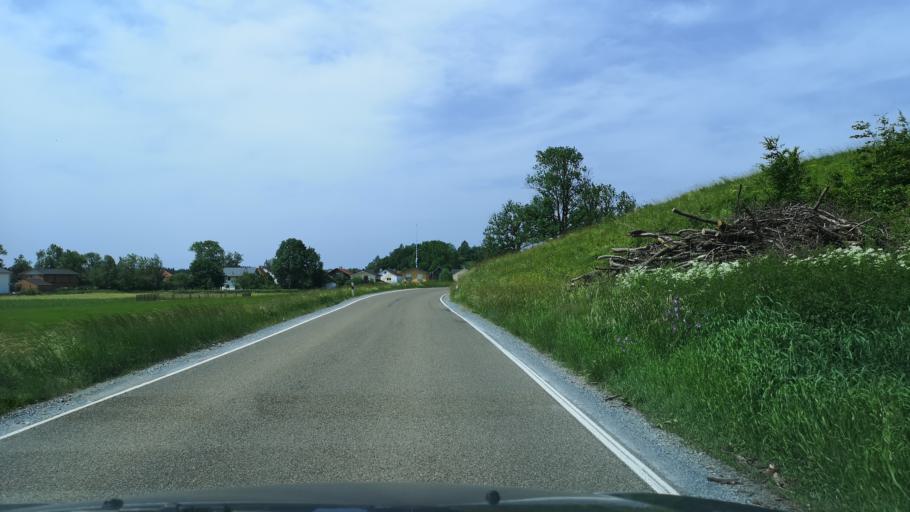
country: DE
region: Bavaria
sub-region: Upper Bavaria
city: Anzing
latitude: 48.1312
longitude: 11.8377
